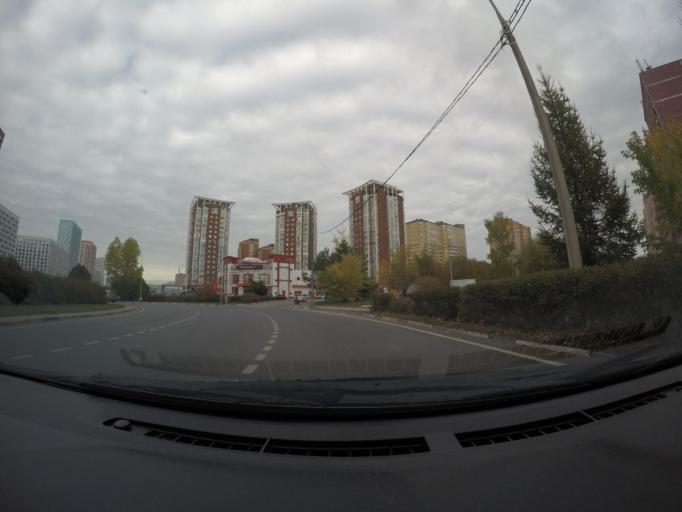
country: RU
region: Moskovskaya
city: Mytishchi
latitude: 55.9171
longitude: 37.7257
